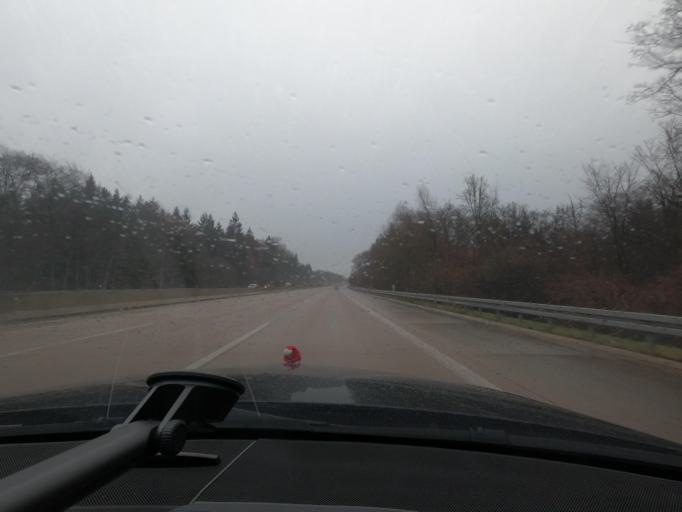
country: DE
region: Lower Saxony
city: Garlstorf
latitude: 53.2207
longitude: 10.0762
